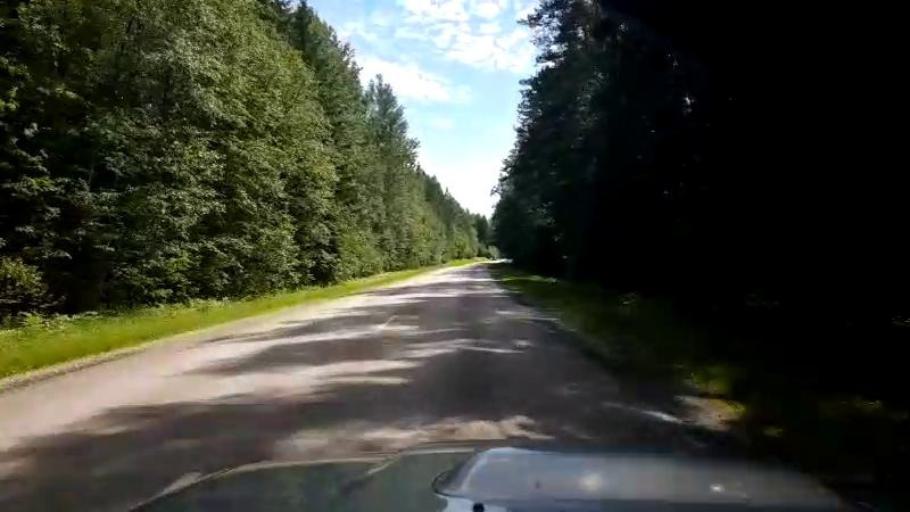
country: EE
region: Laeaene-Virumaa
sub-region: Rakke vald
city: Rakke
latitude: 58.8771
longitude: 26.2956
